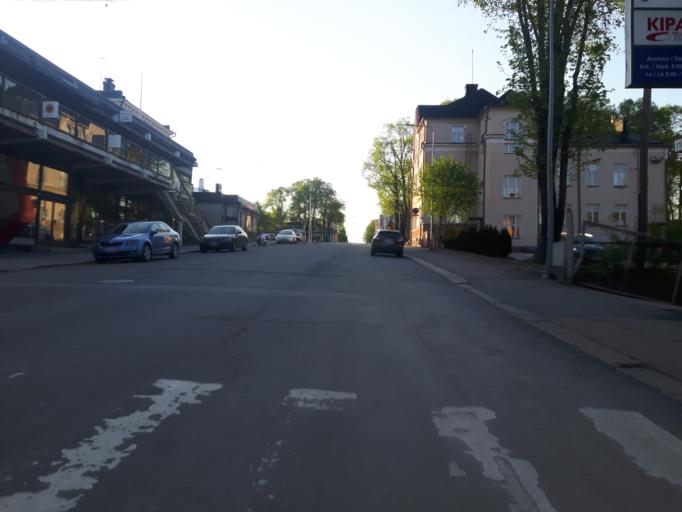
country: FI
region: Uusimaa
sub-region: Loviisa
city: Lovisa
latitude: 60.4563
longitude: 26.2270
